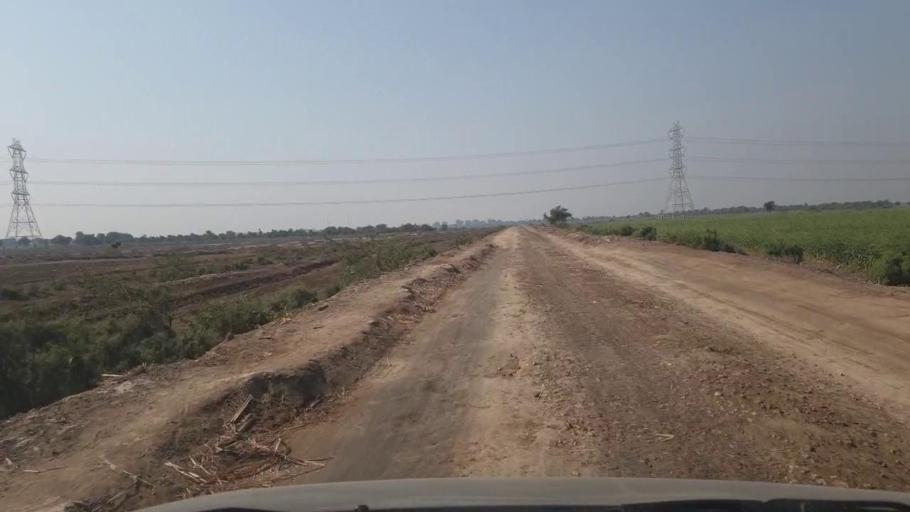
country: PK
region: Sindh
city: Mirwah Gorchani
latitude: 25.2439
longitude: 69.1002
